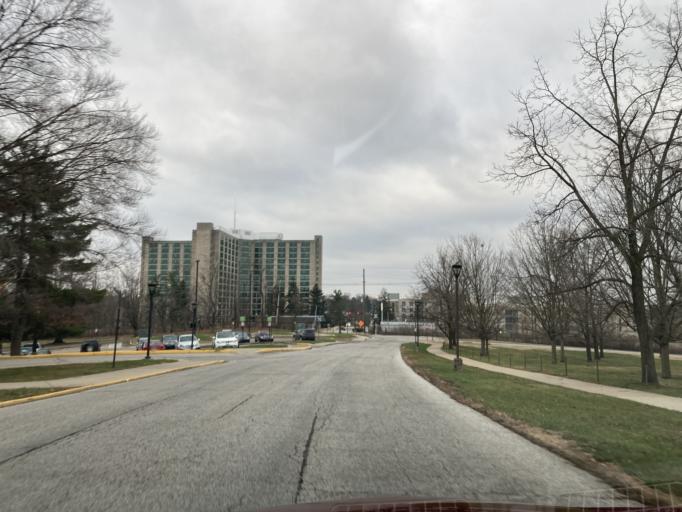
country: US
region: Indiana
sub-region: Monroe County
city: Bloomington
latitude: 39.1734
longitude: -86.5097
